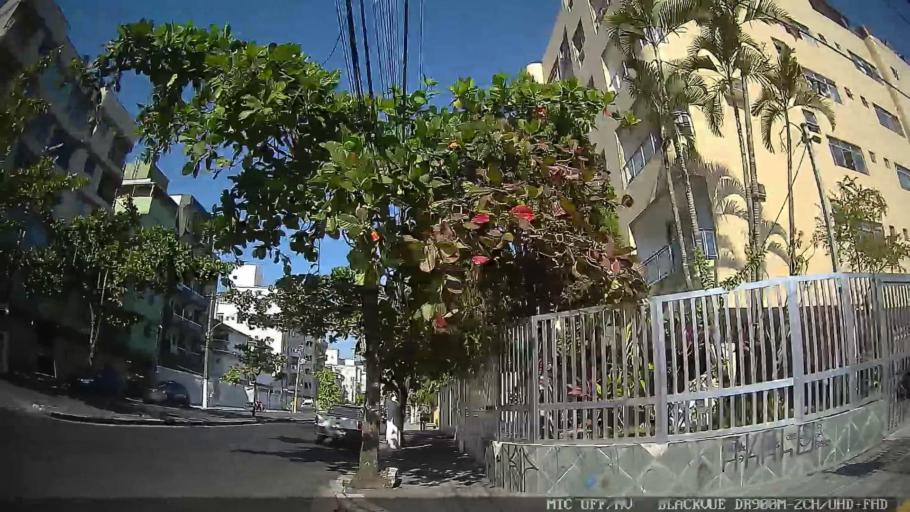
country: BR
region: Sao Paulo
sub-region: Guaruja
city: Guaruja
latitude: -24.0067
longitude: -46.2744
